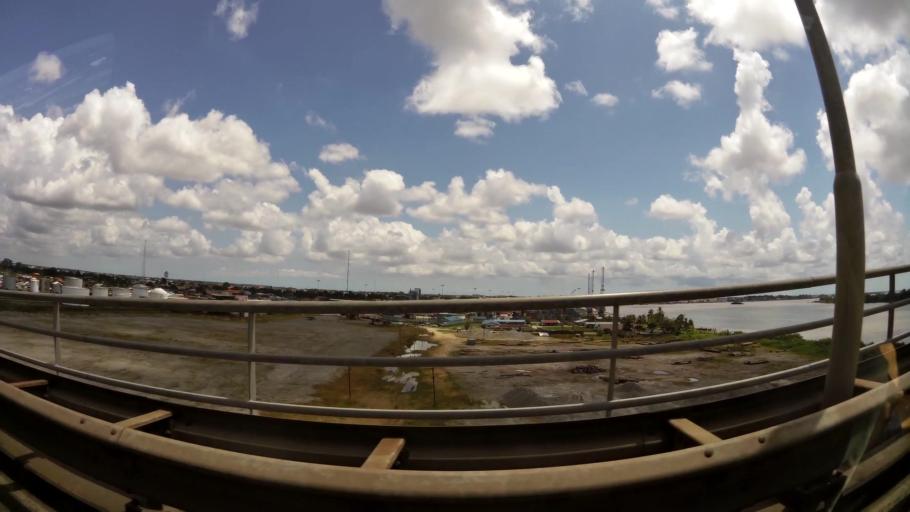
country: SR
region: Paramaribo
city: Paramaribo
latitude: 5.8054
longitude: -55.1679
